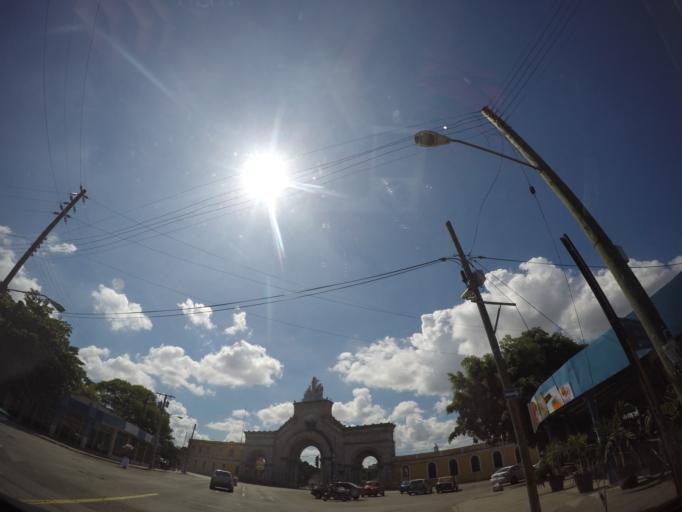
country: CU
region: La Habana
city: Guanabacoa
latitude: 23.0943
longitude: -82.3155
